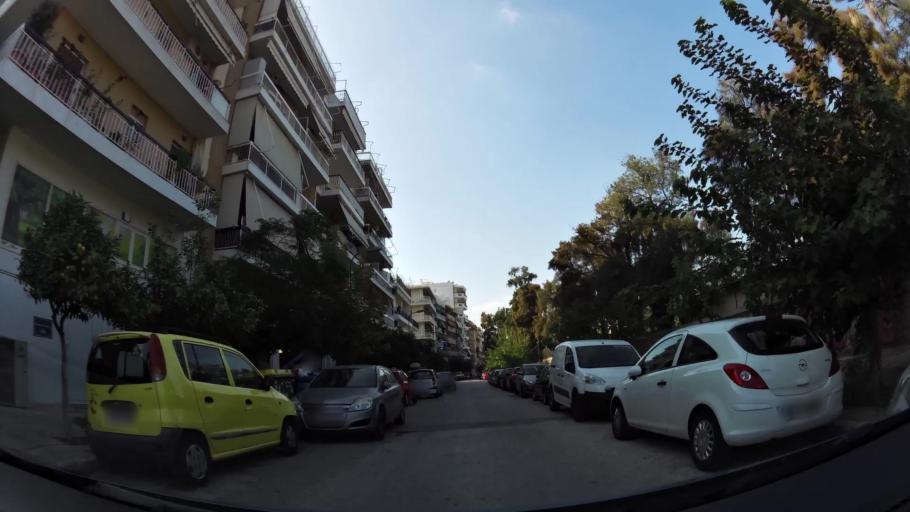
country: GR
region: Attica
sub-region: Nomarchia Athinas
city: Kaisariani
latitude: 37.9847
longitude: 23.7705
